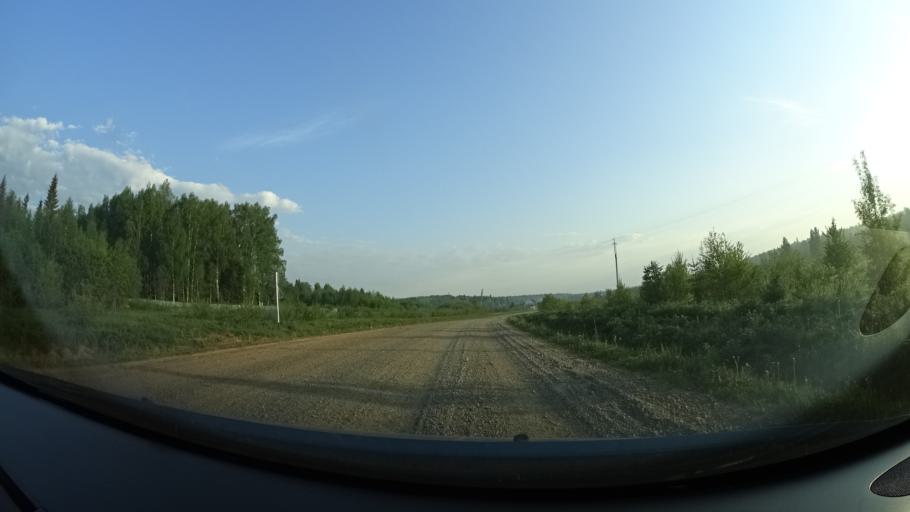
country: RU
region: Perm
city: Kuyeda
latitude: 56.6099
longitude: 55.7121
